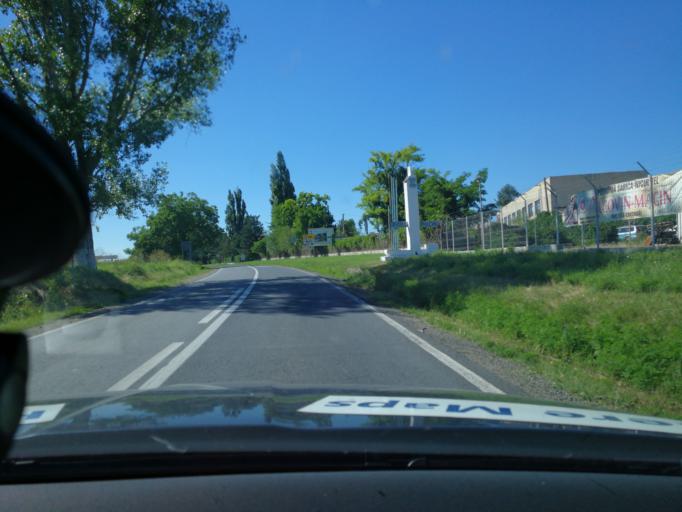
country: RO
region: Tulcea
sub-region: Oras Macin
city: Macin
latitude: 45.2388
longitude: 28.1527
